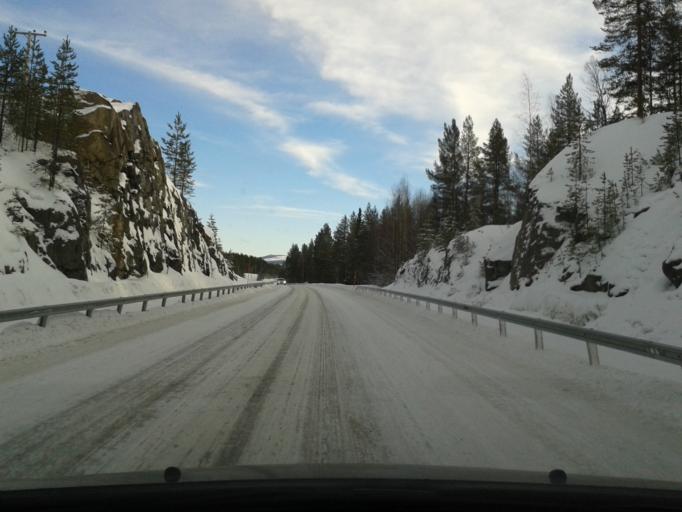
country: SE
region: Vaesterbotten
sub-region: Asele Kommun
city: Asele
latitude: 64.3562
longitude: 16.9739
